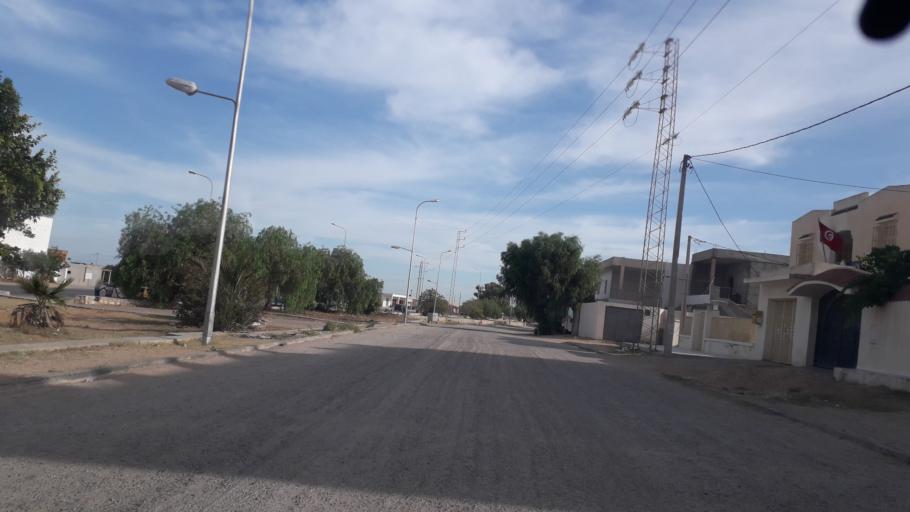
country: TN
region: Safaqis
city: Al Qarmadah
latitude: 34.8867
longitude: 10.7619
